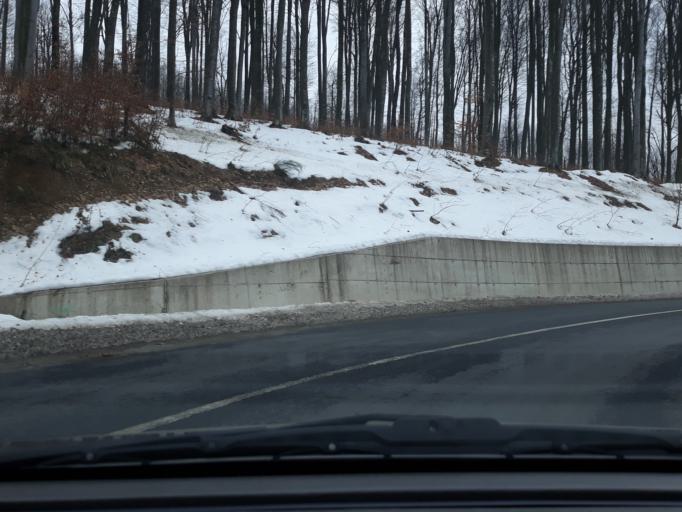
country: RO
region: Bihor
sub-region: Oras Alesd
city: Padurea Neagra
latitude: 47.1211
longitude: 22.4275
